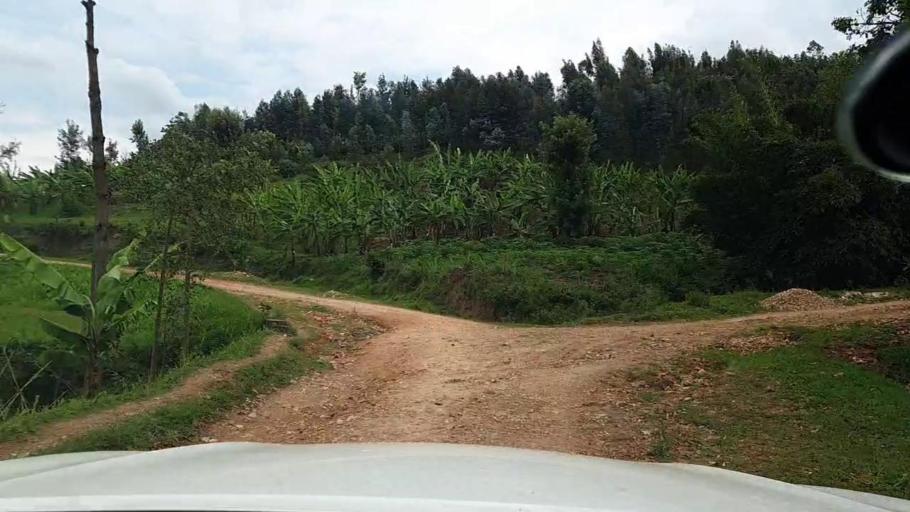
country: RW
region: Western Province
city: Kibuye
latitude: -2.0778
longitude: 29.4221
